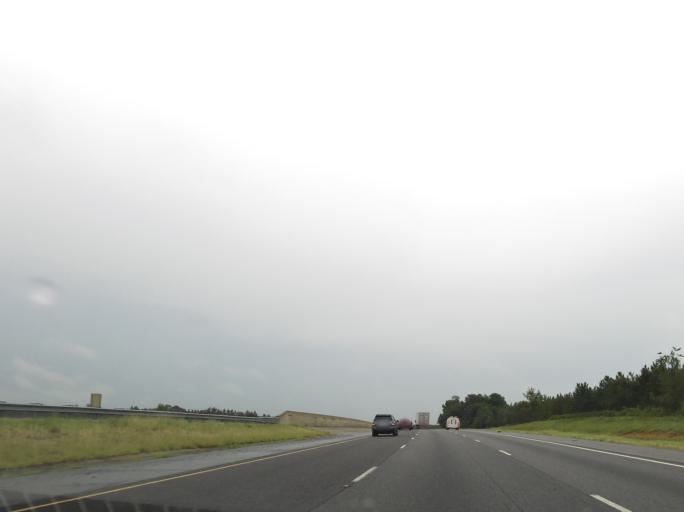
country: US
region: Georgia
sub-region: Turner County
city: Ashburn
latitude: 31.8076
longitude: -83.7065
